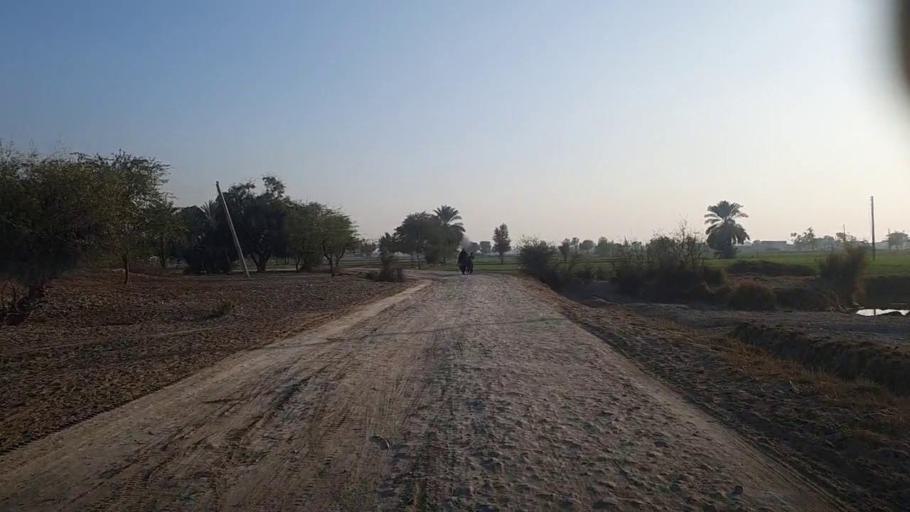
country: PK
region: Sindh
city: Khairpur
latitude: 28.0684
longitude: 69.7510
